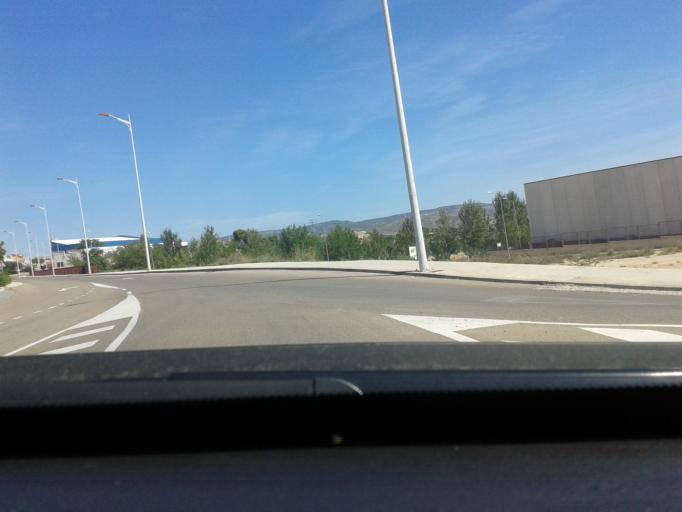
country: ES
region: Castille-La Mancha
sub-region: Provincia de Albacete
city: Caudete
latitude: 38.7087
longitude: -0.9793
